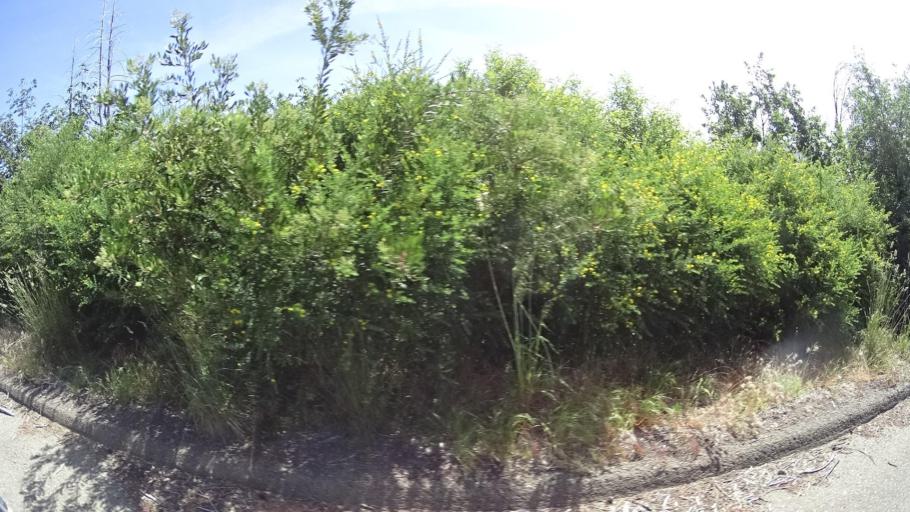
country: US
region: California
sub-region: Lake County
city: Cobb
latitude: 38.7831
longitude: -122.7064
